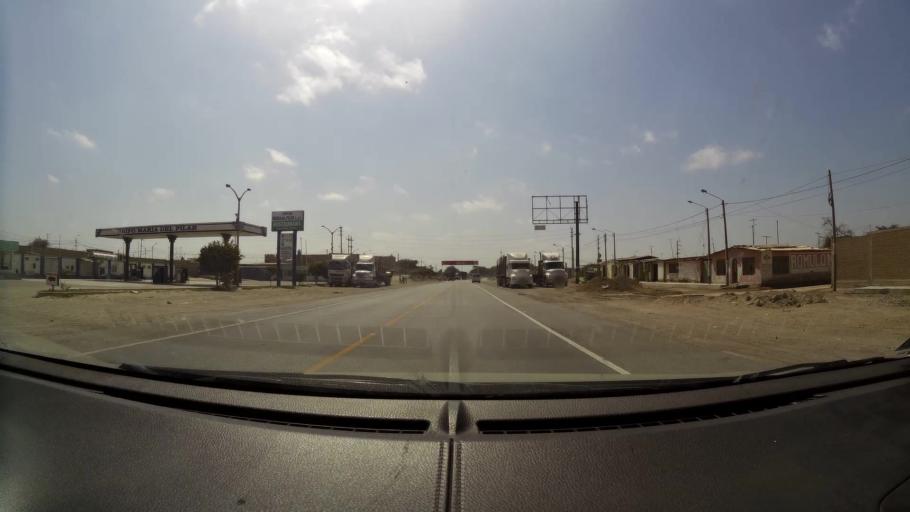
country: PE
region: Lambayeque
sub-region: Provincia de Chiclayo
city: Reque
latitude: -6.8799
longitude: -79.8141
